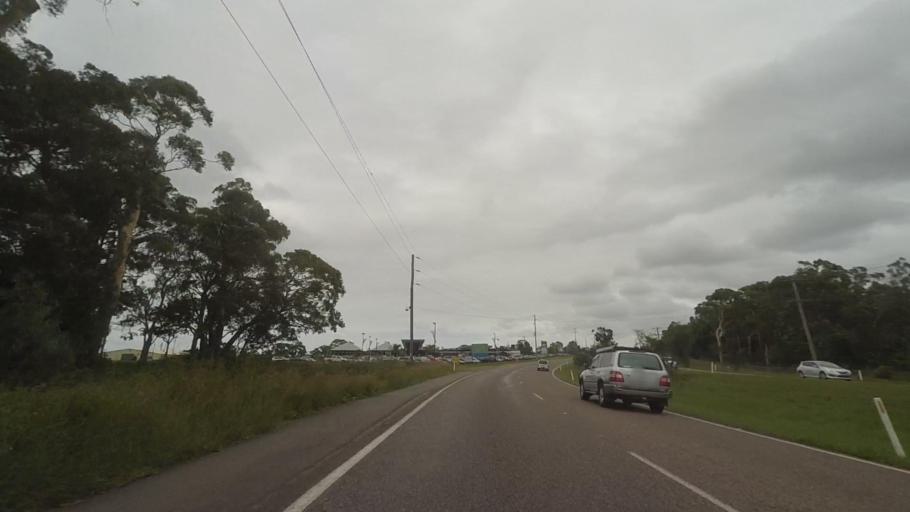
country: AU
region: New South Wales
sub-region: Wyong Shire
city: Buff Point
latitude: -33.1955
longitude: 151.5264
